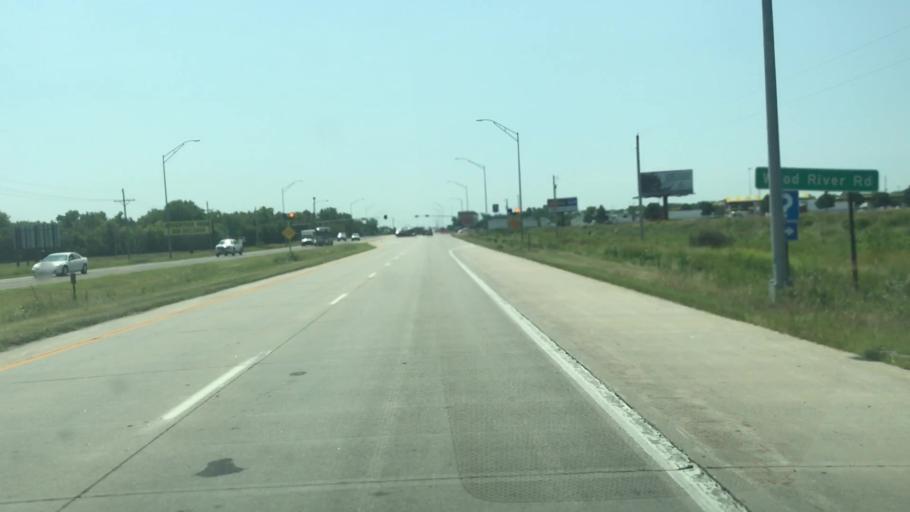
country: US
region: Nebraska
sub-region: Hall County
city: Grand Island
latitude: 40.8344
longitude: -98.3786
